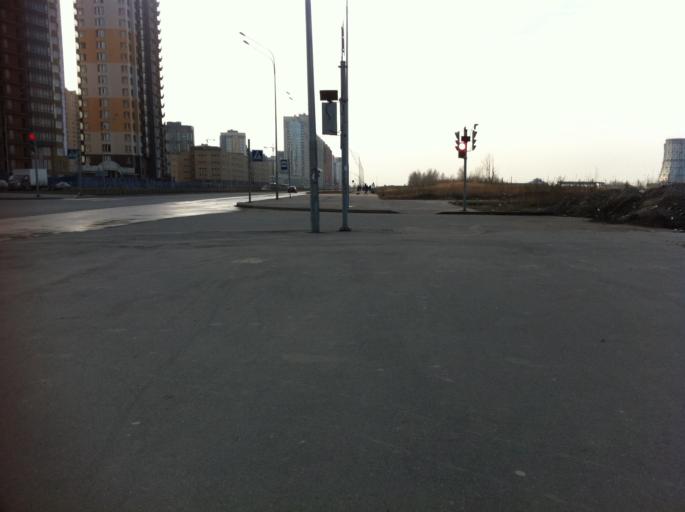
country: RU
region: St.-Petersburg
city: Uritsk
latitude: 59.8633
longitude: 30.1929
